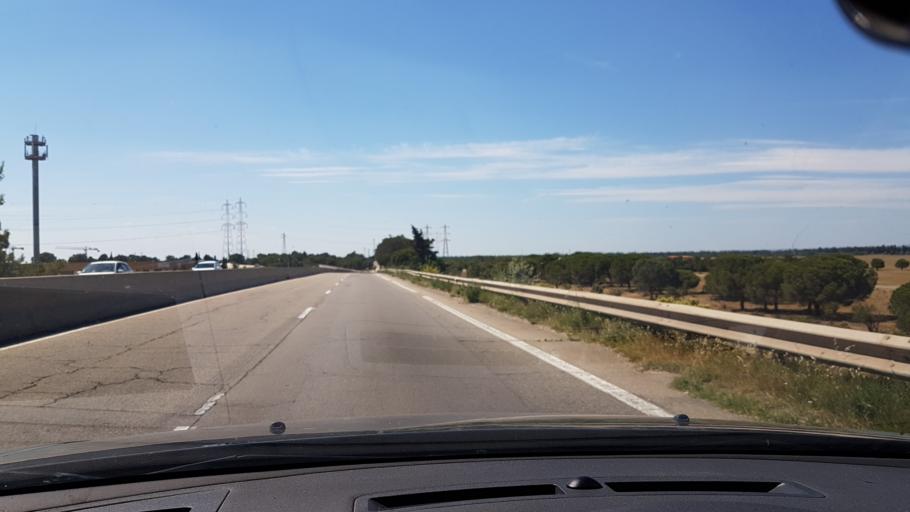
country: FR
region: Provence-Alpes-Cote d'Azur
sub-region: Departement des Bouches-du-Rhone
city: Fos-sur-Mer
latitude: 43.4745
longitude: 4.9023
